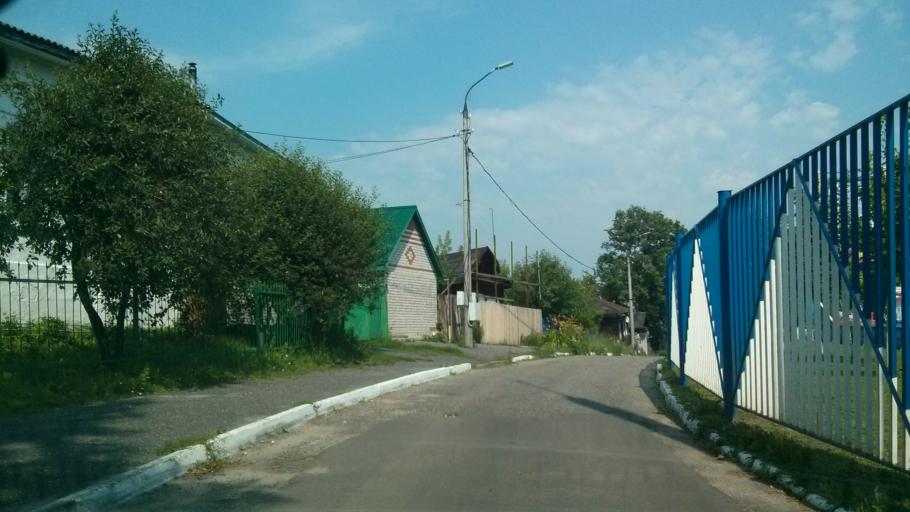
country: RU
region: Vladimir
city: Murom
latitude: 55.5797
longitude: 42.0582
